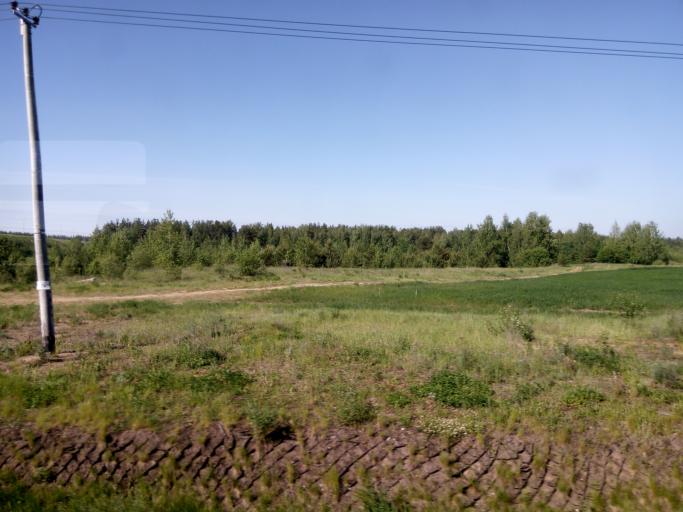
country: RU
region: Tatarstan
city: Stolbishchi
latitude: 55.6845
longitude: 49.2015
